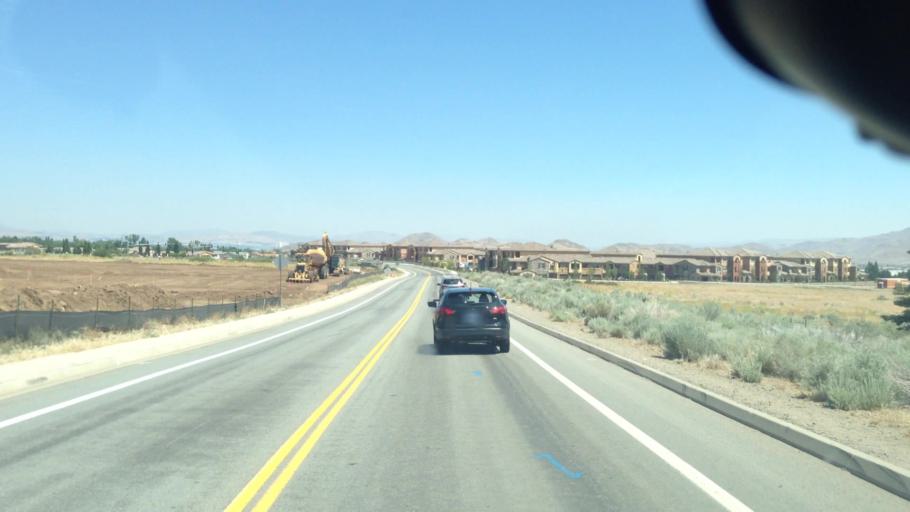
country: US
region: Nevada
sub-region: Washoe County
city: Sparks
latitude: 39.4043
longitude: -119.7597
